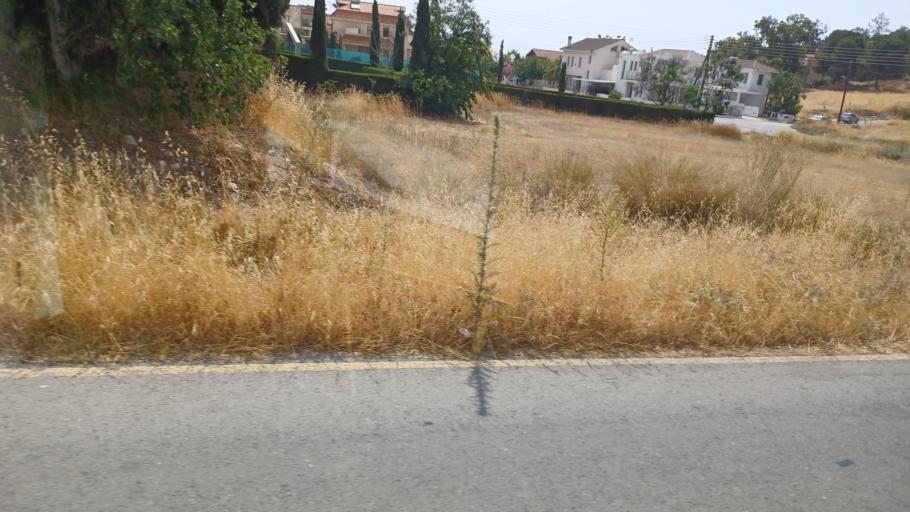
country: CY
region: Larnaka
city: Aradippou
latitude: 34.9480
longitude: 33.5697
